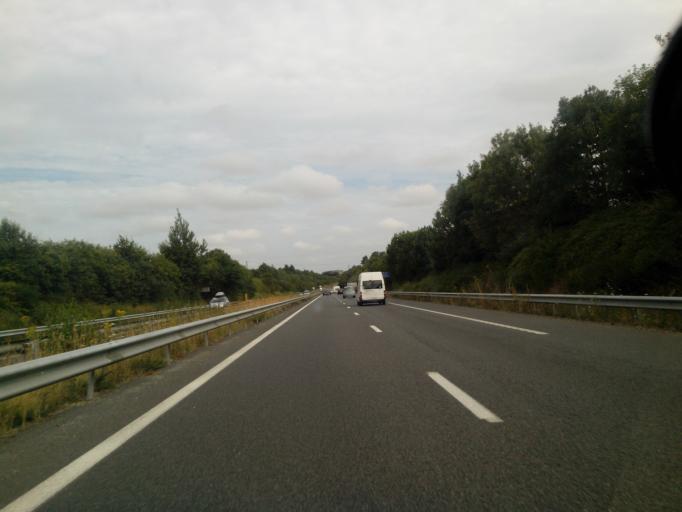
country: FR
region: Brittany
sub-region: Departement du Morbihan
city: Nivillac
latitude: 47.5077
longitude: -2.2711
